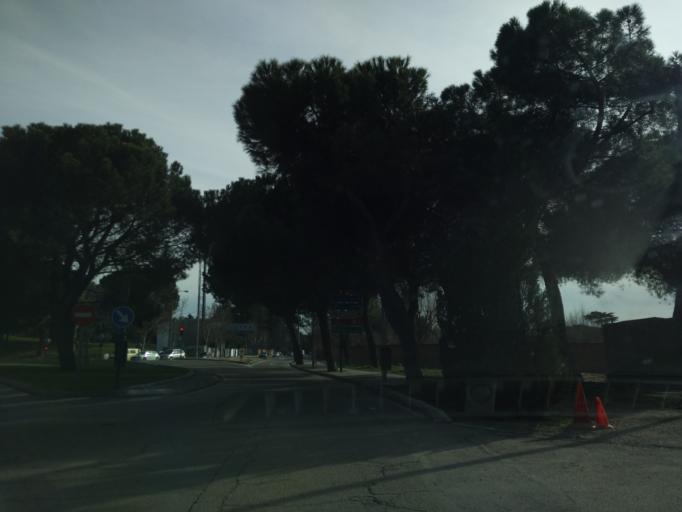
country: ES
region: Madrid
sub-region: Provincia de Madrid
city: Tetuan de las Victorias
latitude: 40.4603
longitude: -3.7295
